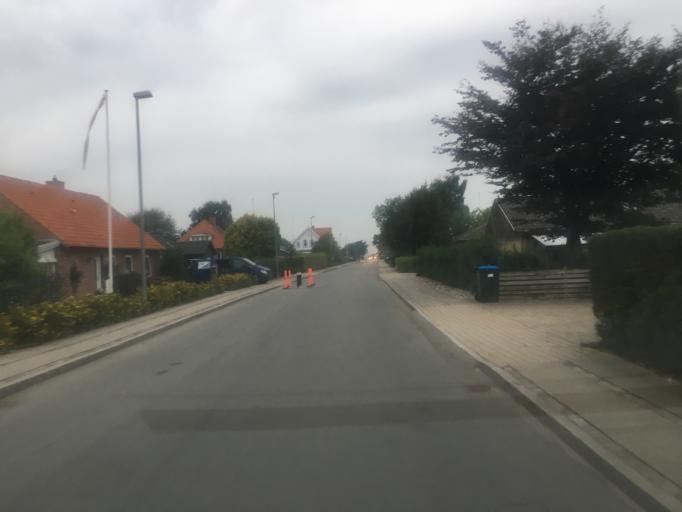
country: DE
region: Schleswig-Holstein
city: Aventoft
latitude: 54.9469
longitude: 8.8021
